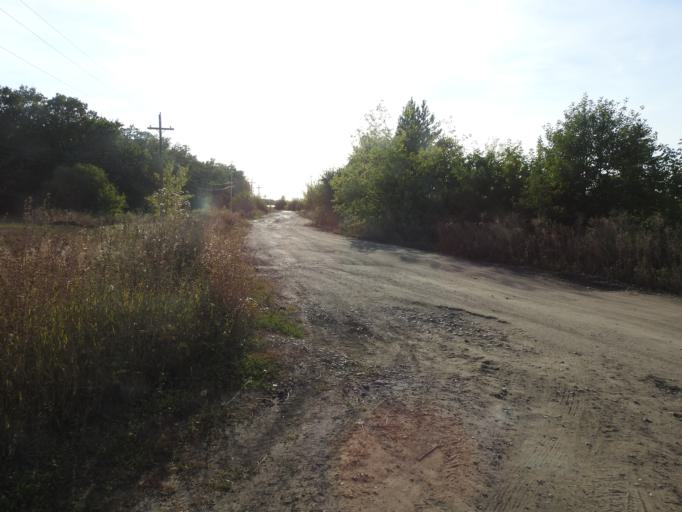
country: RU
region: Saratov
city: Novyye Burasy
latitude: 52.2070
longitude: 46.1324
